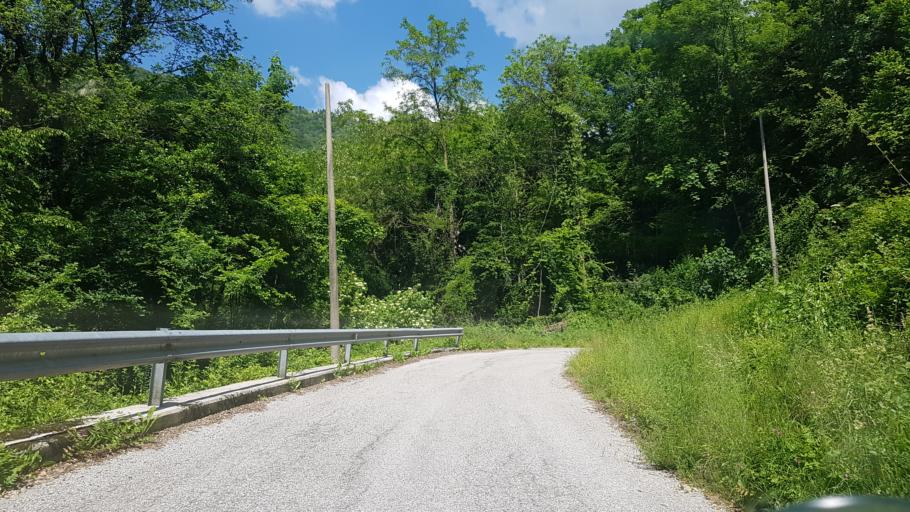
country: IT
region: Friuli Venezia Giulia
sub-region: Provincia di Udine
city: Torreano
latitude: 46.1660
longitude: 13.4307
